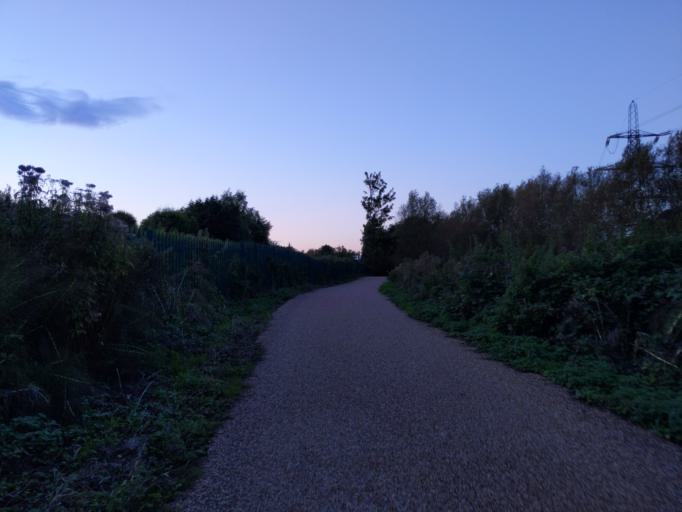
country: GB
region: England
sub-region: Oxfordshire
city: Radley
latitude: 51.7191
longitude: -1.2432
